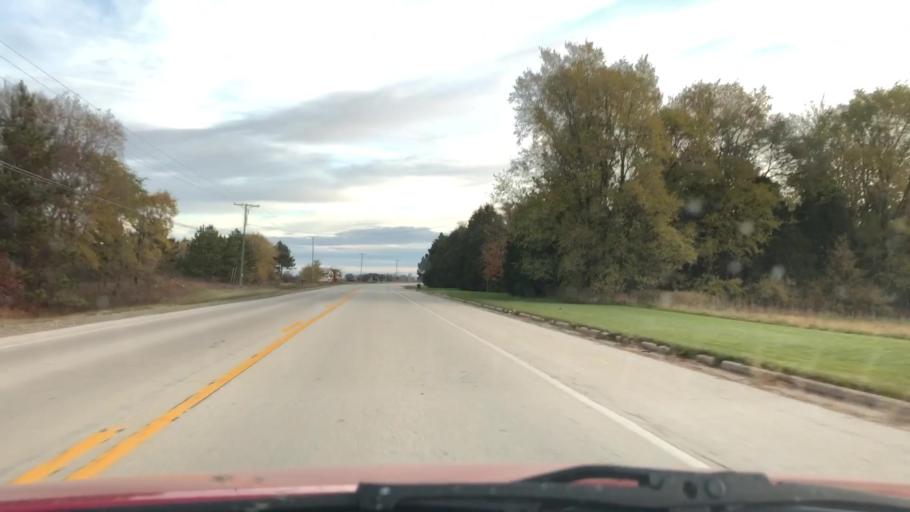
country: US
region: Wisconsin
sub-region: Brown County
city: Oneida
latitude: 44.4178
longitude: -88.2535
